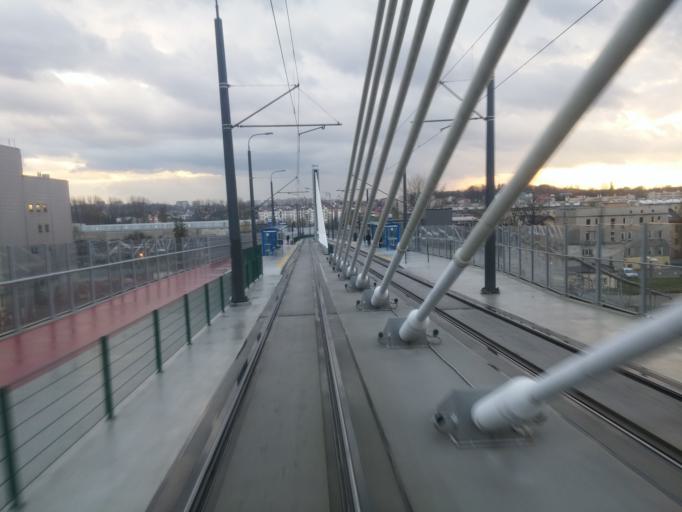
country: PL
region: Lesser Poland Voivodeship
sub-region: Krakow
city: Krakow
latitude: 50.0339
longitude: 19.9777
